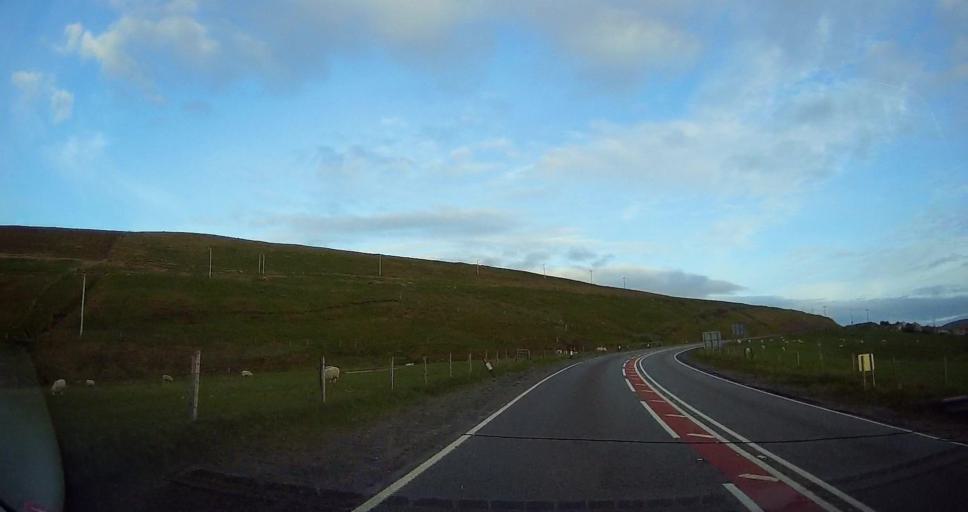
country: GB
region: Scotland
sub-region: Shetland Islands
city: Lerwick
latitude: 60.1855
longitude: -1.2251
